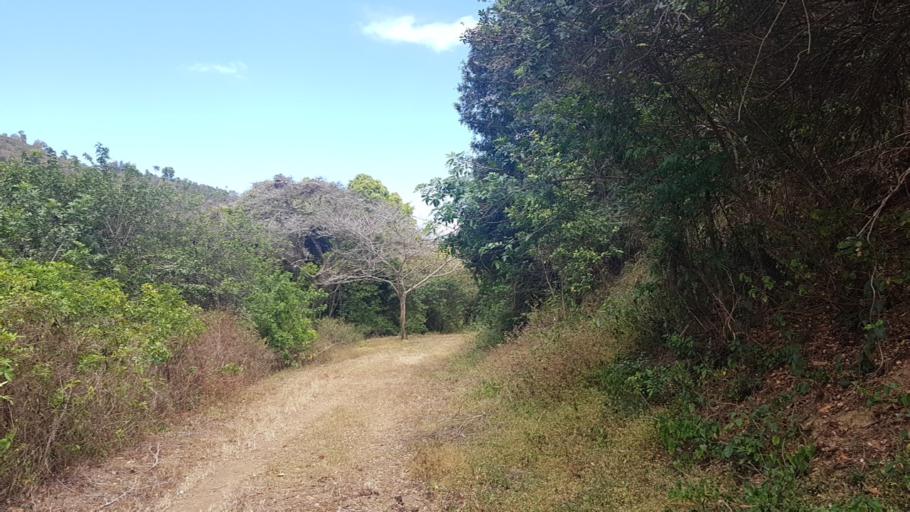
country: NC
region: South Province
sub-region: Dumbea
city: Dumbea
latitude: -22.1764
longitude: 166.4731
